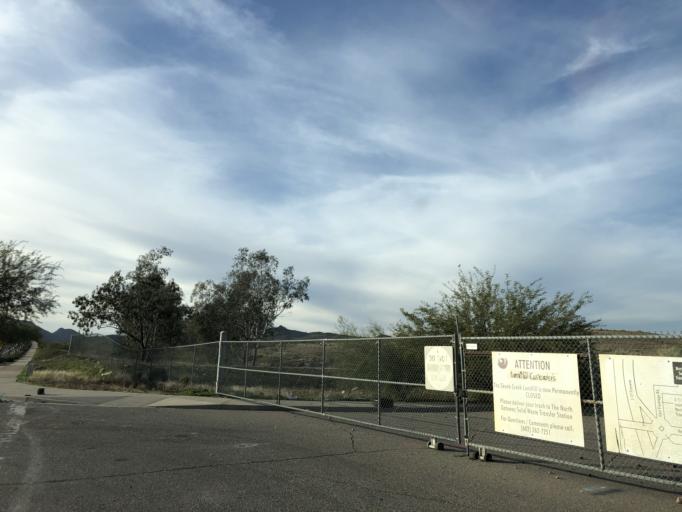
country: US
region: Arizona
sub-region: Maricopa County
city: Anthem
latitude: 33.7131
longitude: -112.1224
